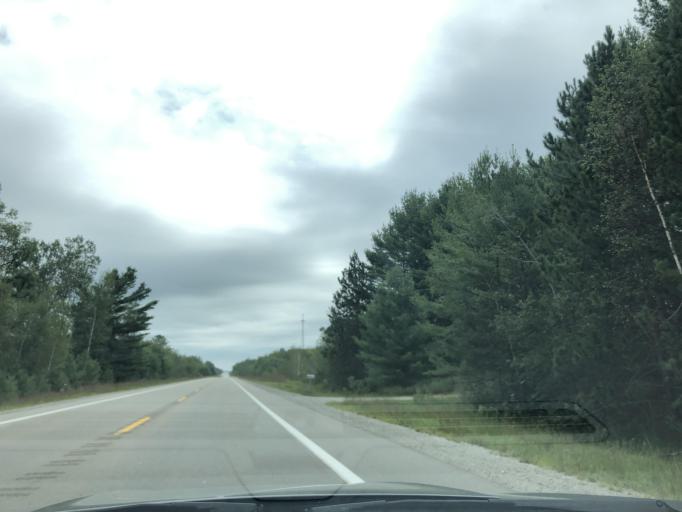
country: US
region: Michigan
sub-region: Clare County
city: Harrison
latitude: 44.0311
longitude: -84.9827
